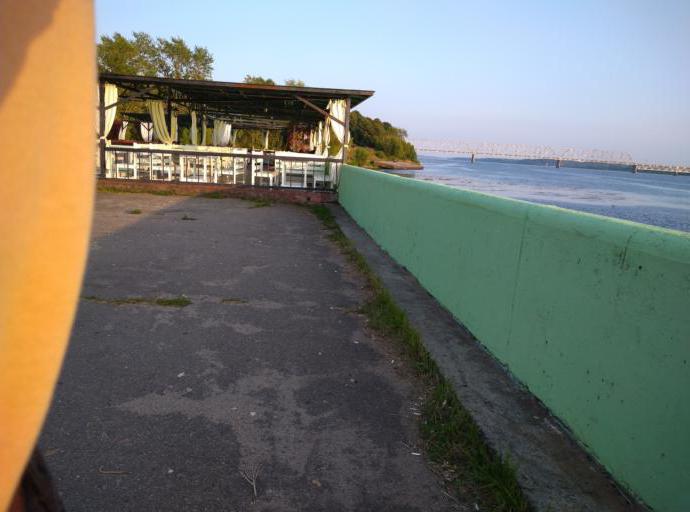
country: RU
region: Kostroma
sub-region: Kostromskoy Rayon
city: Kostroma
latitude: 57.7496
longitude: 40.9525
